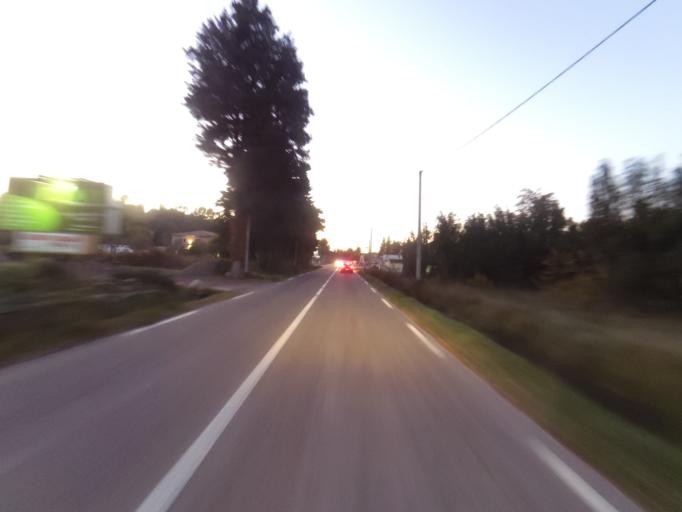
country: FR
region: Provence-Alpes-Cote d'Azur
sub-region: Departement du Vaucluse
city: Carpentras
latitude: 44.0634
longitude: 5.0329
